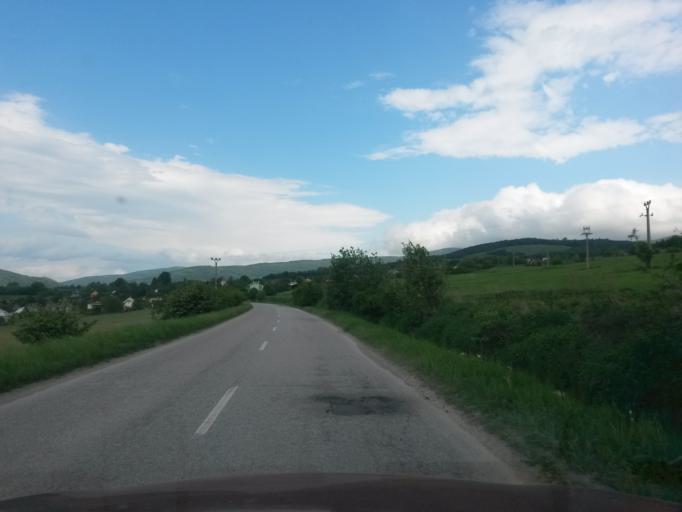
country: SK
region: Kosicky
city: Kosice
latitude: 48.7293
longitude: 21.1136
